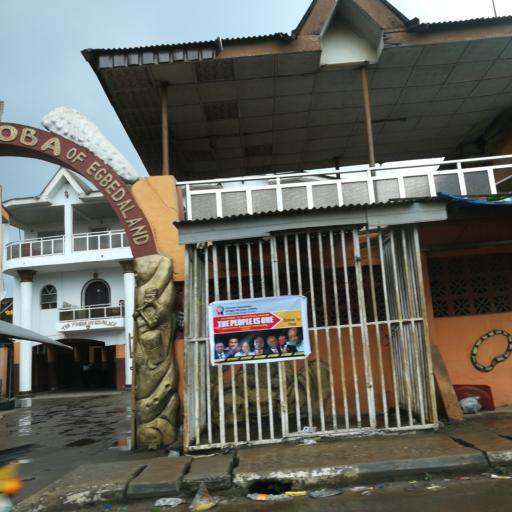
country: NG
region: Lagos
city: Agege
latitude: 6.5959
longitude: 3.2929
